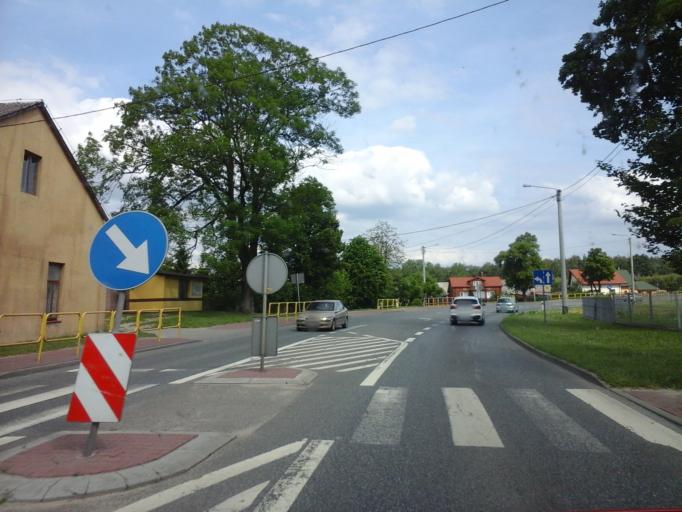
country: PL
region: Lodz Voivodeship
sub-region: Powiat opoczynski
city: Paradyz
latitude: 51.3053
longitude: 20.1158
